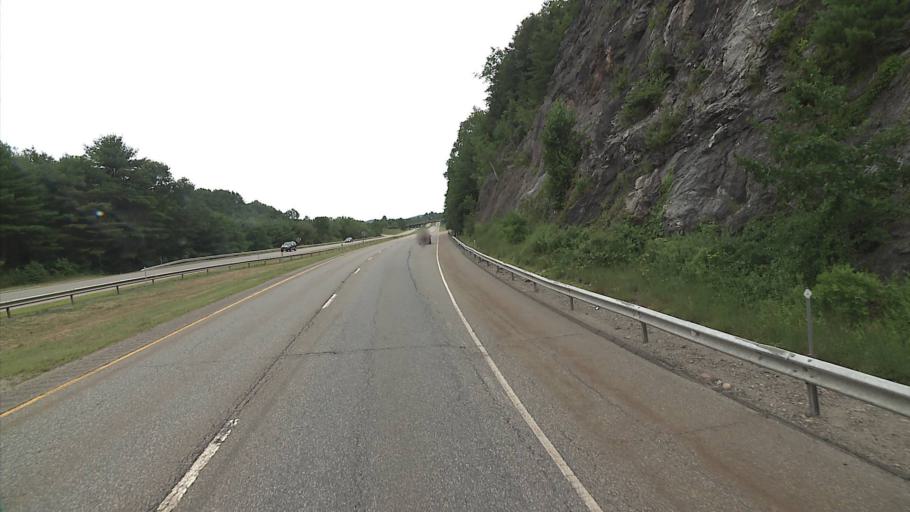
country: US
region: Connecticut
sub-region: Litchfield County
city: Northwest Harwinton
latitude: 41.7574
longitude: -73.1154
